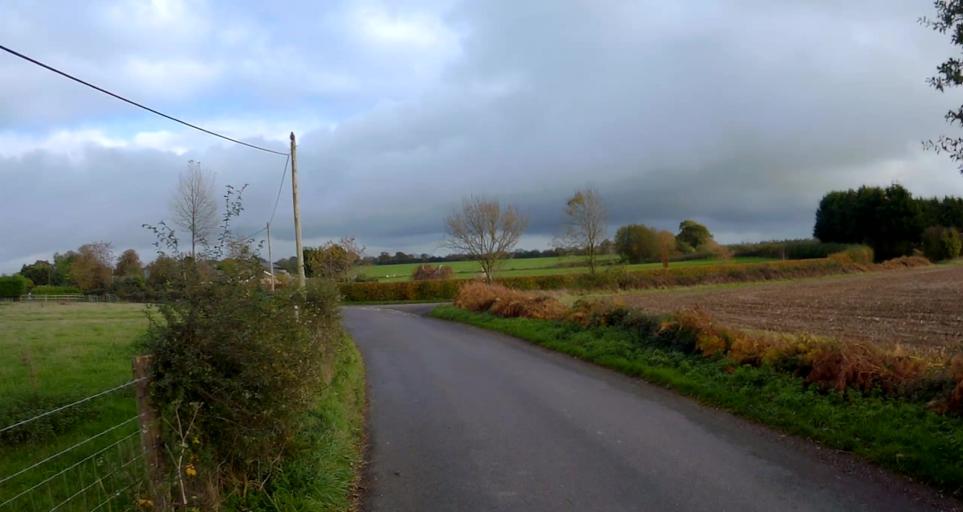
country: GB
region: England
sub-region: Hampshire
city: Four Marks
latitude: 51.1360
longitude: -1.1067
